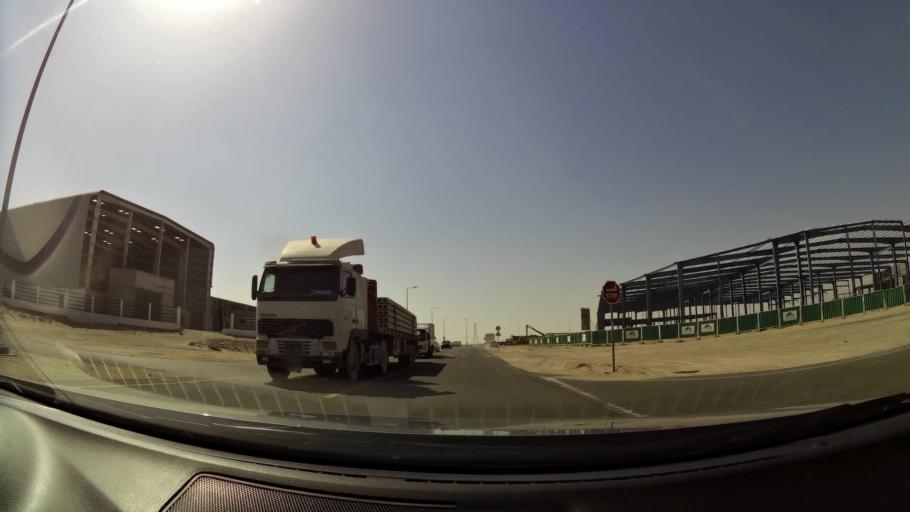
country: AE
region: Dubai
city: Dubai
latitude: 24.9130
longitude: 55.0705
